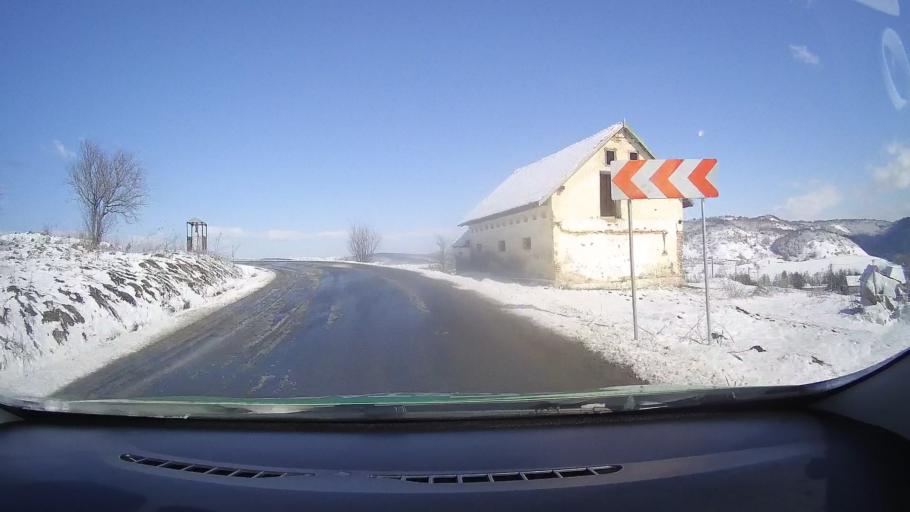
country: RO
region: Sibiu
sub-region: Comuna Rosia
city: Rosia
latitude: 45.7979
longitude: 24.3865
